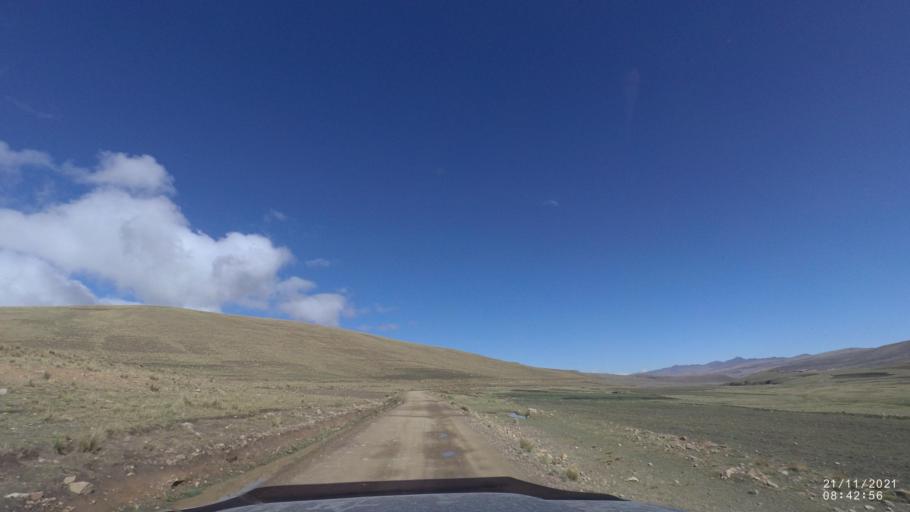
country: BO
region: Cochabamba
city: Cochabamba
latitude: -17.2636
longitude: -66.2226
